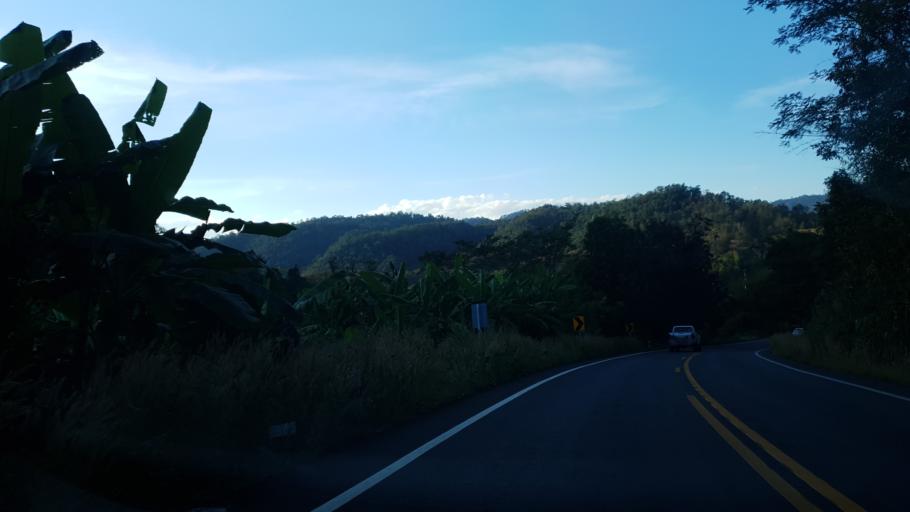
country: TH
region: Loei
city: Dan Sai
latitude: 17.2297
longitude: 101.0566
